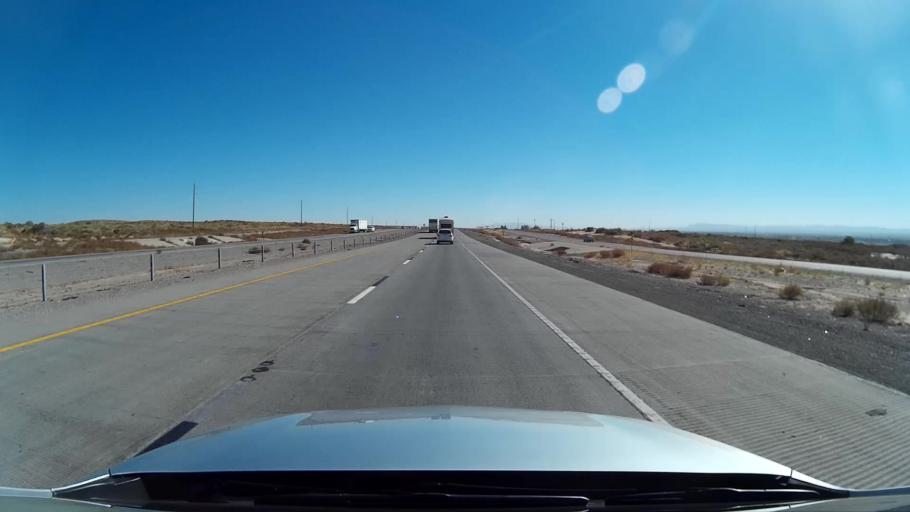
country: US
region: Texas
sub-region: El Paso County
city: Sparks
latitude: 31.6268
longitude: -106.2145
